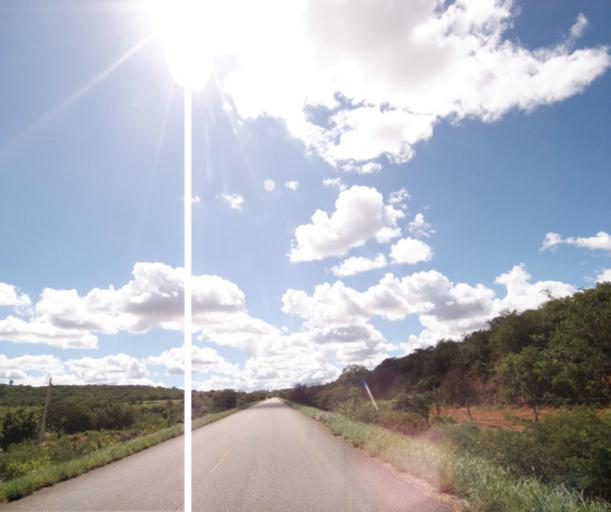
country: BR
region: Bahia
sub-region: Caetite
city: Caetite
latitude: -14.1723
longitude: -42.1987
